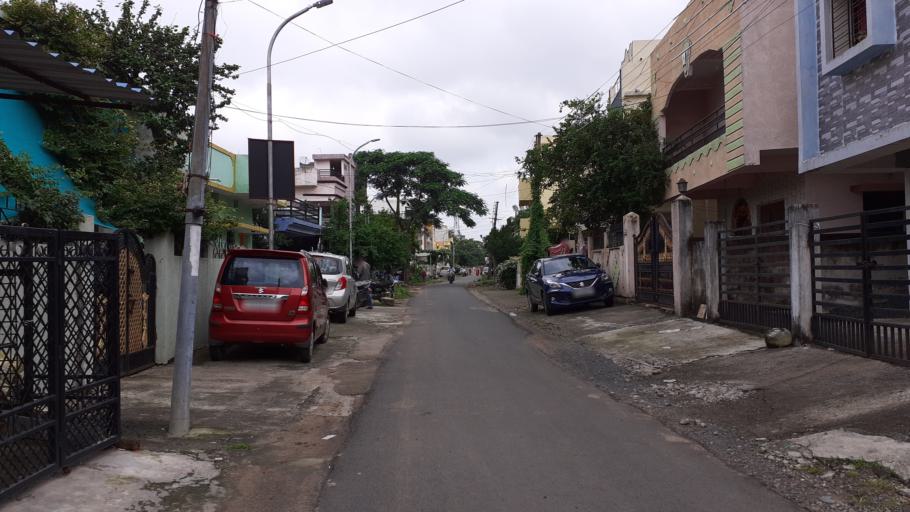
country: IN
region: Maharashtra
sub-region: Nagpur Division
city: Nagpur
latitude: 21.1043
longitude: 79.1144
